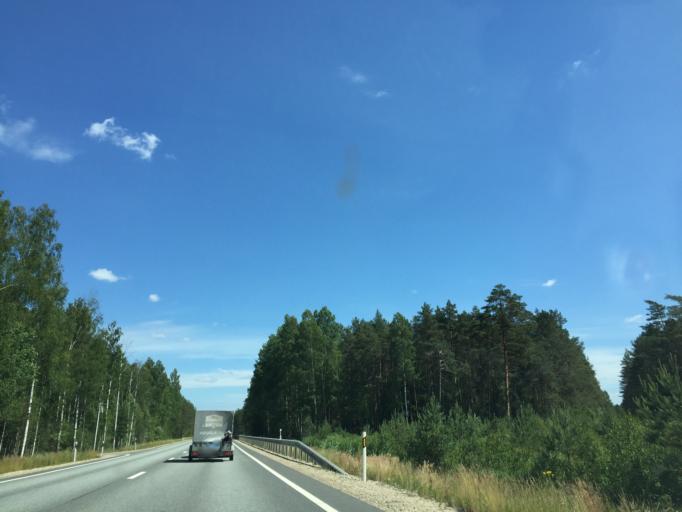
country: LV
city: Tireli
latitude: 56.7990
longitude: 23.4611
